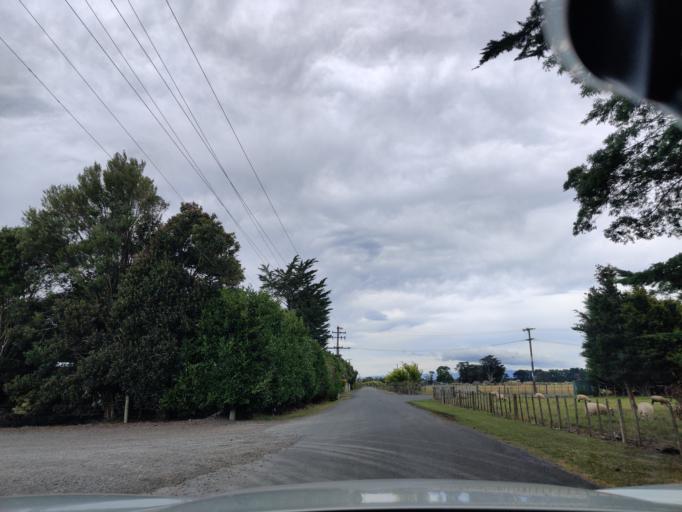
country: NZ
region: Wellington
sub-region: Masterton District
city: Masterton
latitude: -41.0358
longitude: 175.4461
